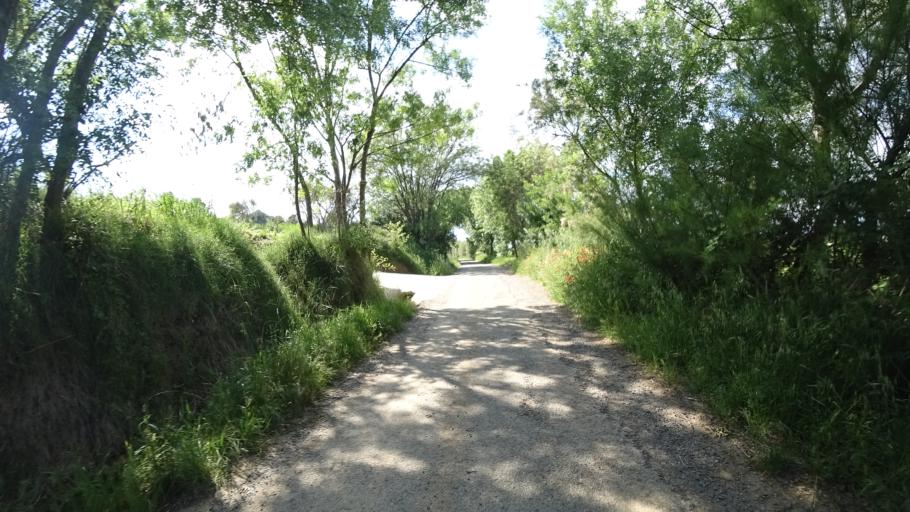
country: FR
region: Languedoc-Roussillon
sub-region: Departement de l'Aude
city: Ginestas
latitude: 43.2640
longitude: 2.8795
